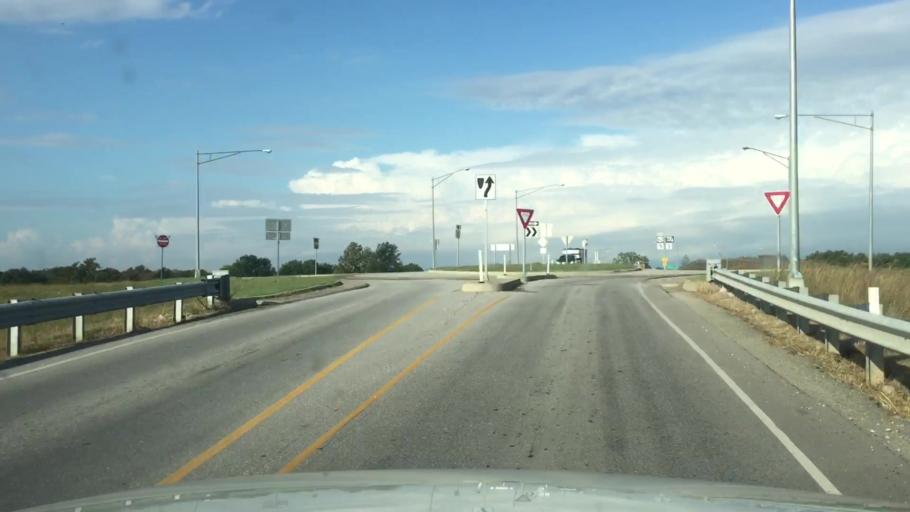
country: US
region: Missouri
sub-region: Boone County
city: Ashland
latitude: 38.8323
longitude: -92.2476
